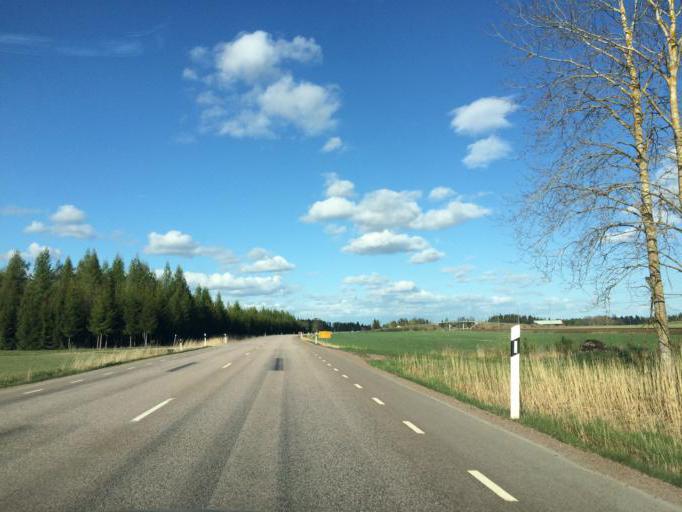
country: SE
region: Vaestmanland
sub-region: Hallstahammars Kommun
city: Kolback
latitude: 59.5509
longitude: 16.1914
